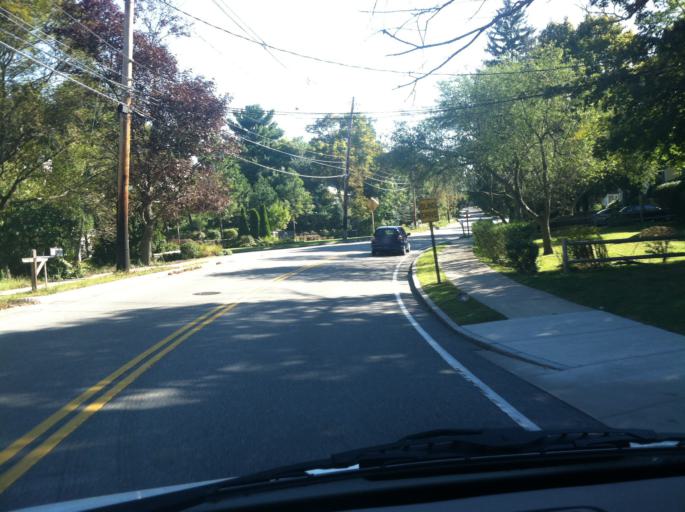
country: US
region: Massachusetts
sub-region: Middlesex County
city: Bedford
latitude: 42.4924
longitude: -71.2901
